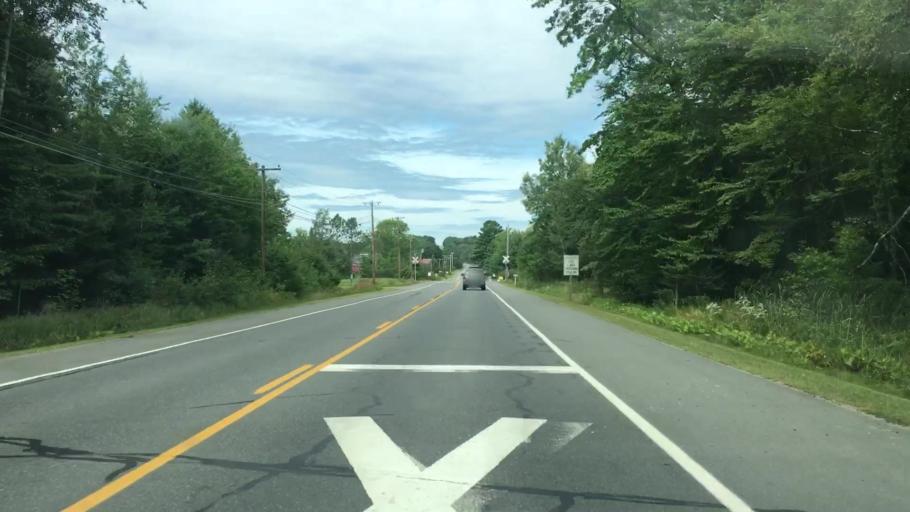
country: US
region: Maine
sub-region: Piscataquis County
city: Milo
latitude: 45.2686
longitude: -68.9964
